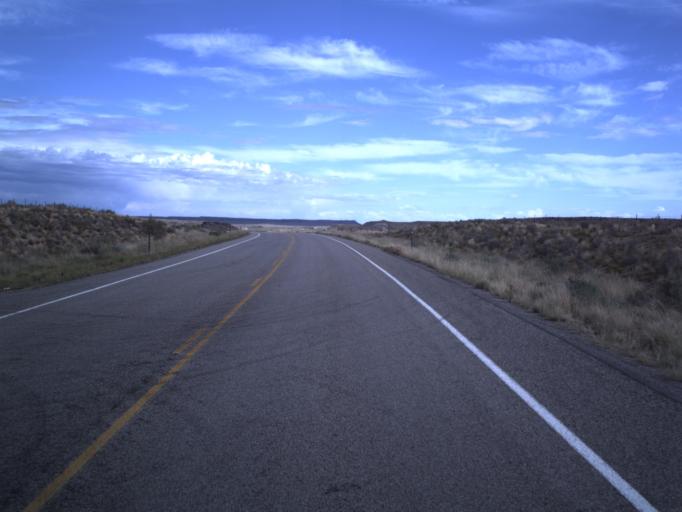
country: US
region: Colorado
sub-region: Montezuma County
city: Towaoc
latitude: 37.1621
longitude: -109.0698
